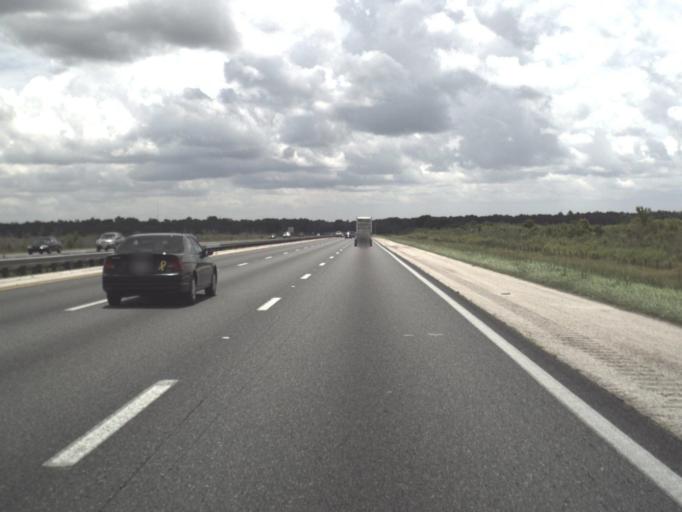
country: US
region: Florida
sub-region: Alachua County
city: Gainesville
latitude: 29.5678
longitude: -82.3500
